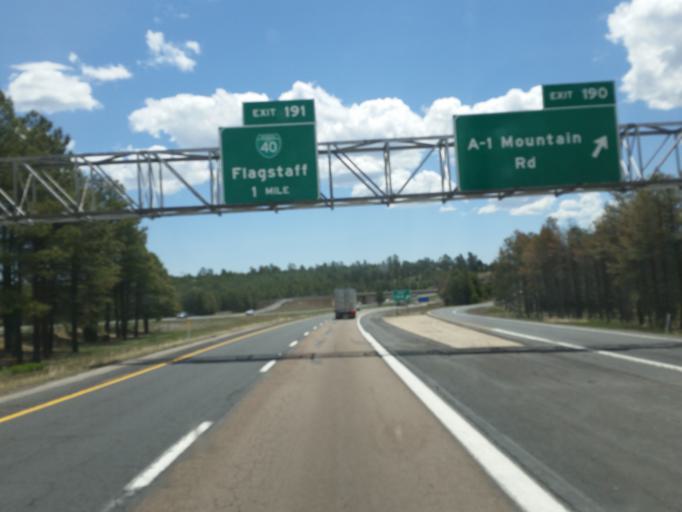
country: US
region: Arizona
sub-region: Coconino County
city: Flagstaff
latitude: 35.1985
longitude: -111.7475
